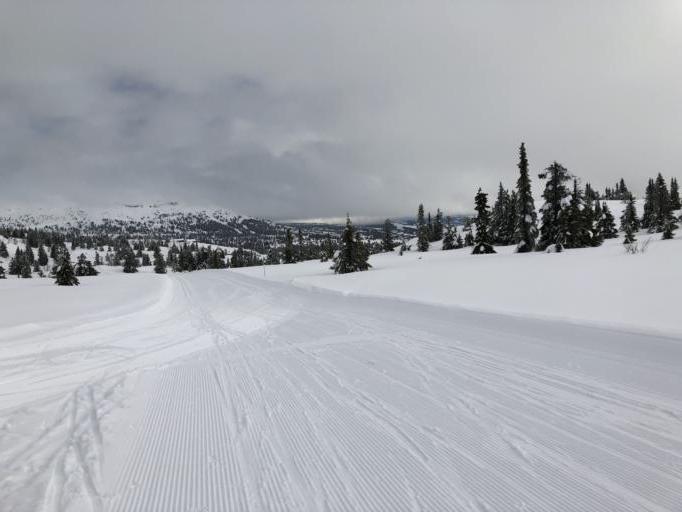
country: NO
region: Oppland
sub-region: Ringebu
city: Ringebu
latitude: 61.3463
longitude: 10.0289
